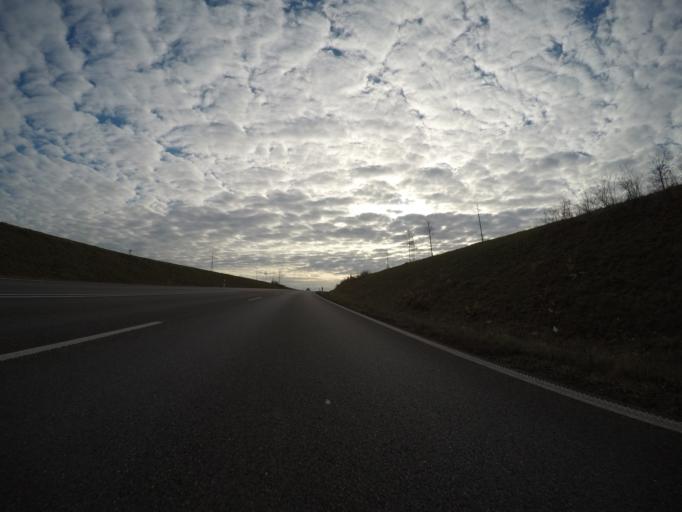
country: DE
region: Thuringia
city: Gossnitz
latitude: 50.8980
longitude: 12.4440
